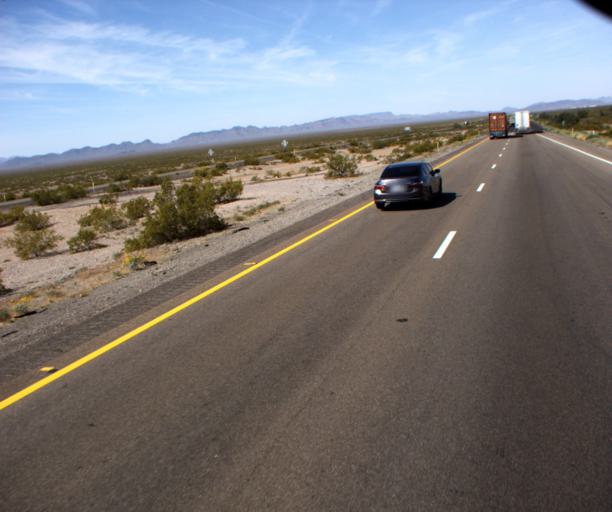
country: US
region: Arizona
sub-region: La Paz County
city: Salome
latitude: 33.6142
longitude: -113.6523
